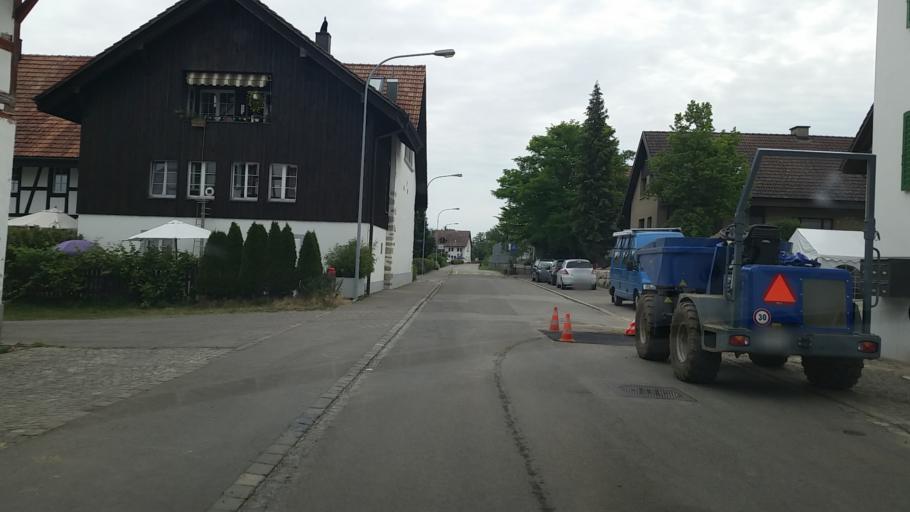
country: CH
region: Zurich
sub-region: Bezirk Dielsdorf
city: Otelfingen
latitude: 47.4980
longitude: 8.3925
